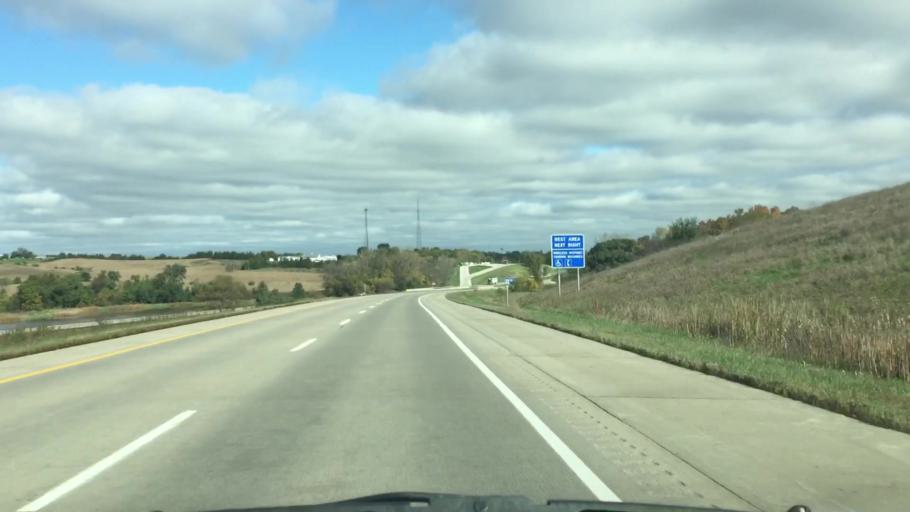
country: US
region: Iowa
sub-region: Clarke County
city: Osceola
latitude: 41.0048
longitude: -93.7978
